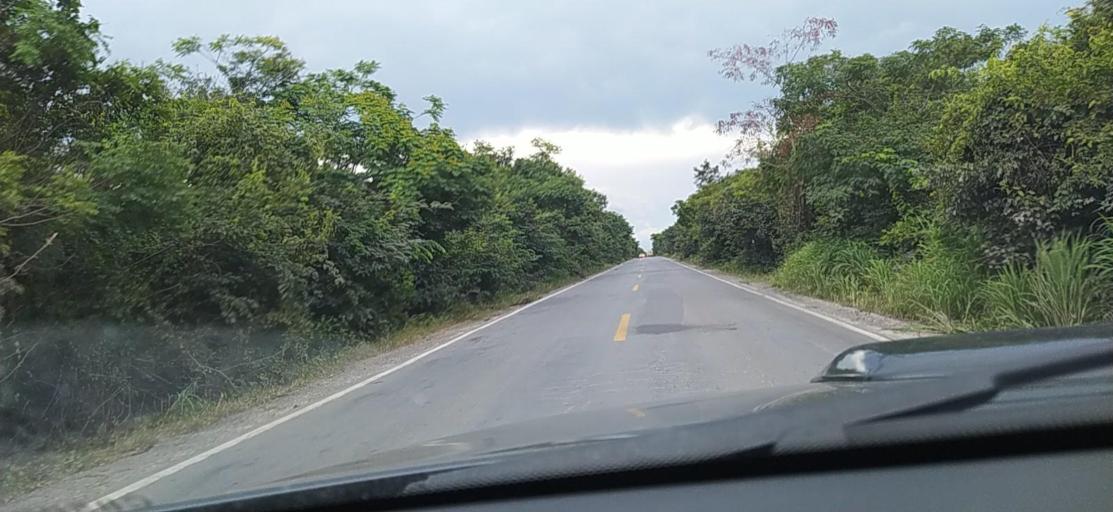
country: BR
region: Minas Gerais
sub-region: Francisco Sa
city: Francisco Sa
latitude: -16.2395
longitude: -43.6217
